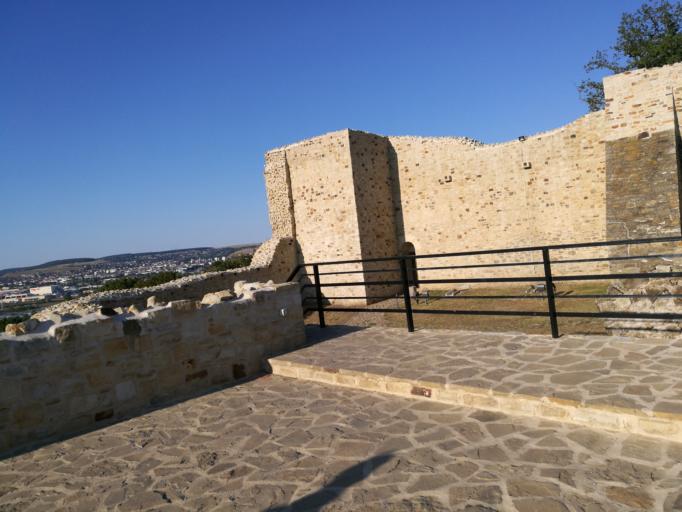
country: RO
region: Suceava
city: Suceava
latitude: 47.6449
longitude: 26.2696
